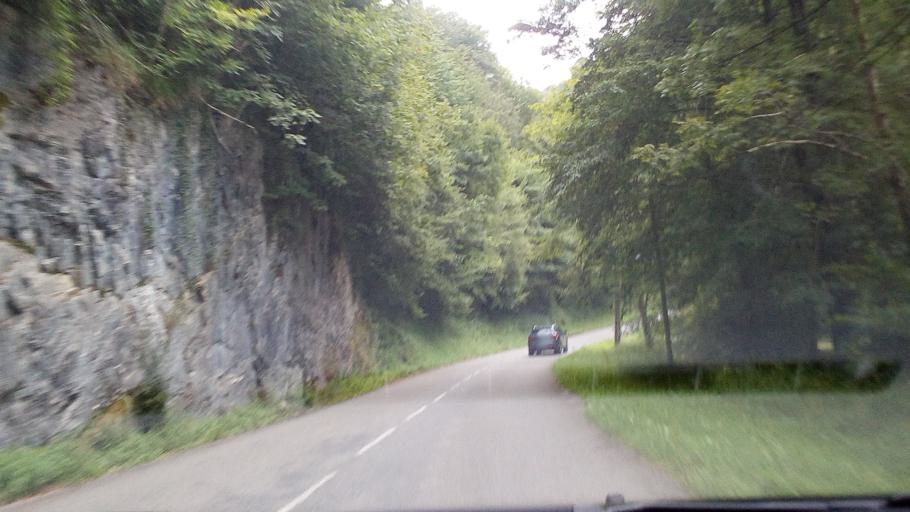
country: FR
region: Aquitaine
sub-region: Departement des Pyrenees-Atlantiques
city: Ogeu-les-Bains
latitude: 43.0815
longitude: -0.5778
